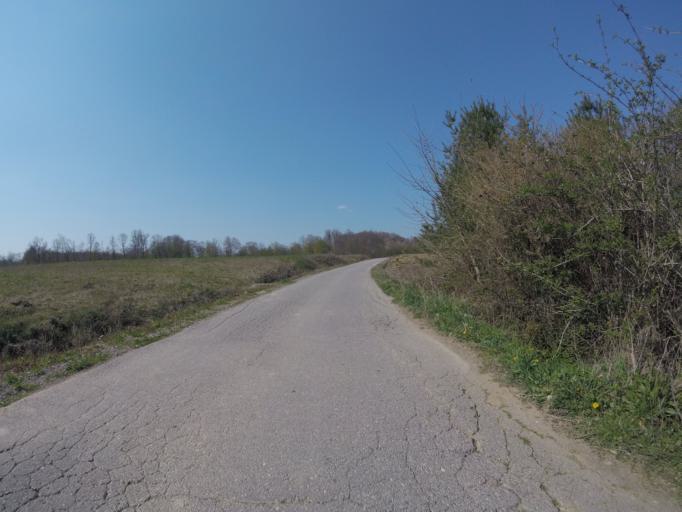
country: HR
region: Grad Zagreb
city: Strmec
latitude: 45.5612
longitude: 15.9063
